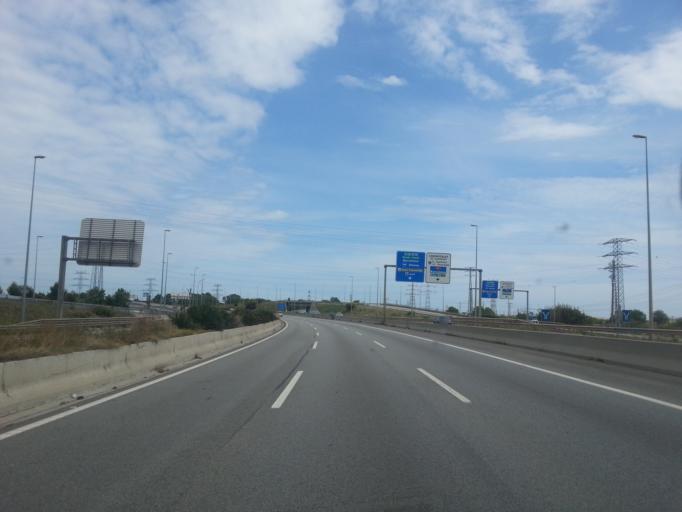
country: ES
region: Catalonia
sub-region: Provincia de Barcelona
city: Cornella de Llobregat
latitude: 41.3423
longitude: 2.0949
